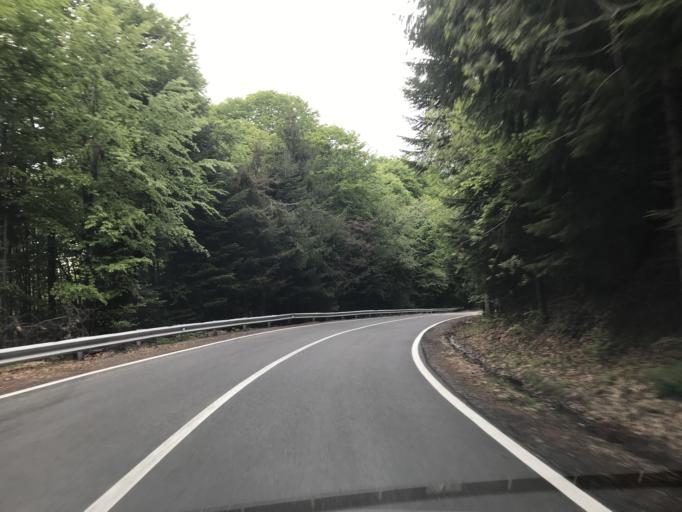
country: RO
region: Sibiu
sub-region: Comuna Cartisoara
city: Cartisoara
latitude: 45.6740
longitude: 24.5898
